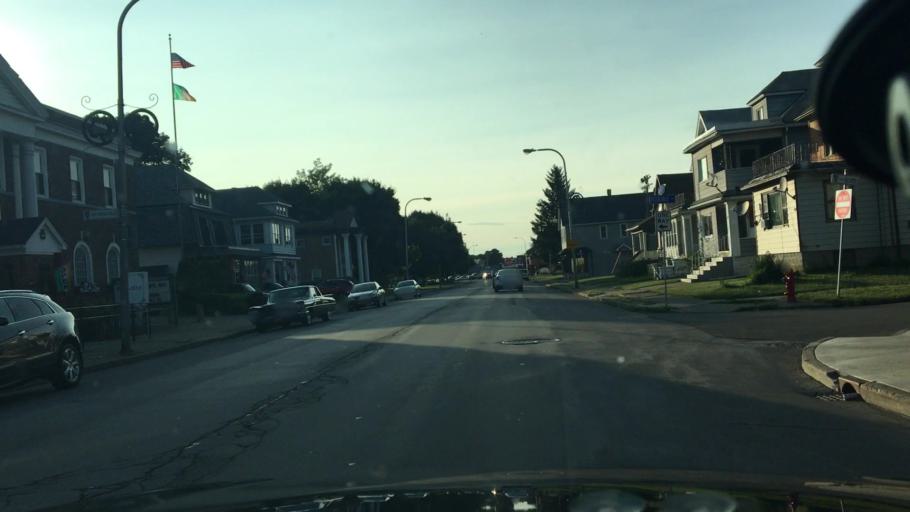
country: US
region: New York
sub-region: Erie County
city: West Seneca
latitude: 42.8543
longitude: -78.8206
